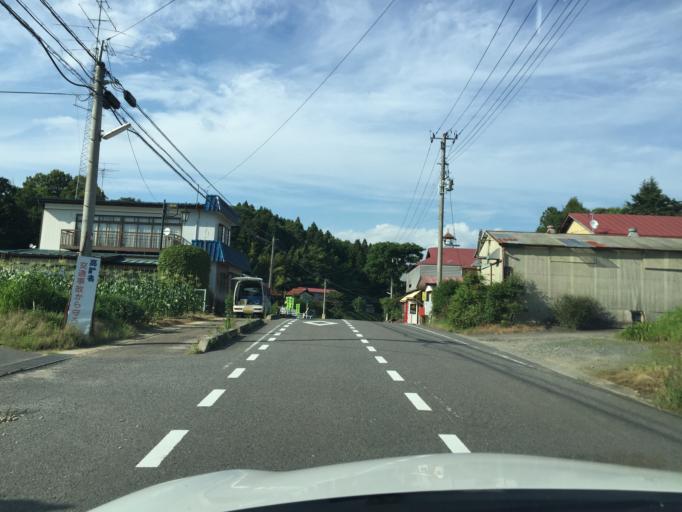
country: JP
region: Fukushima
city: Miharu
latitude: 37.3224
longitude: 140.4876
